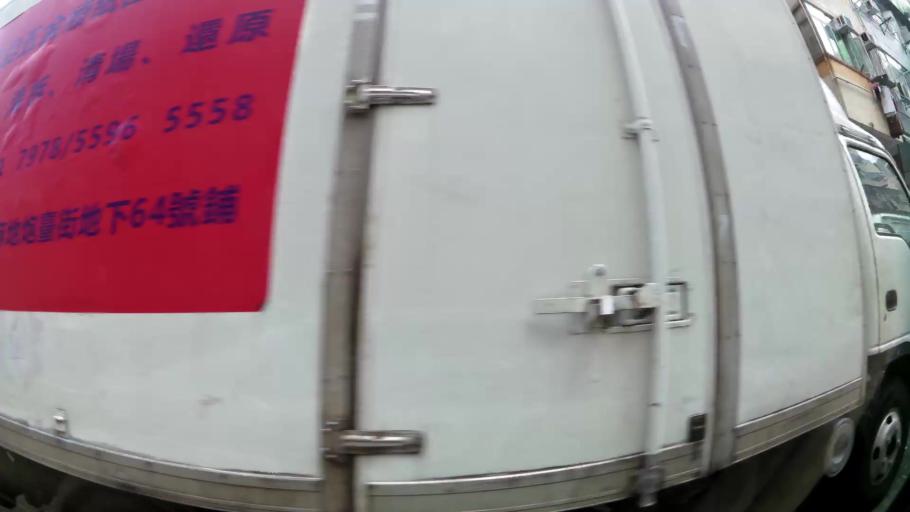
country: HK
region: Kowloon City
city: Kowloon
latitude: 22.3078
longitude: 114.1693
